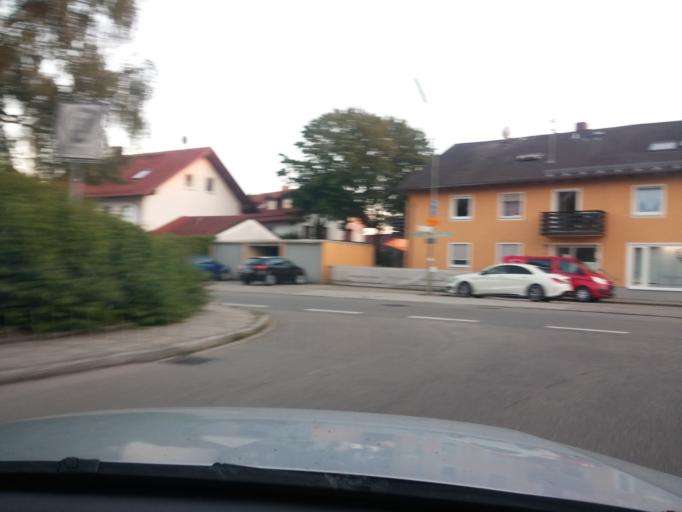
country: DE
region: Bavaria
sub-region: Upper Bavaria
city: Vaterstetten
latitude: 48.1351
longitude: 11.7636
